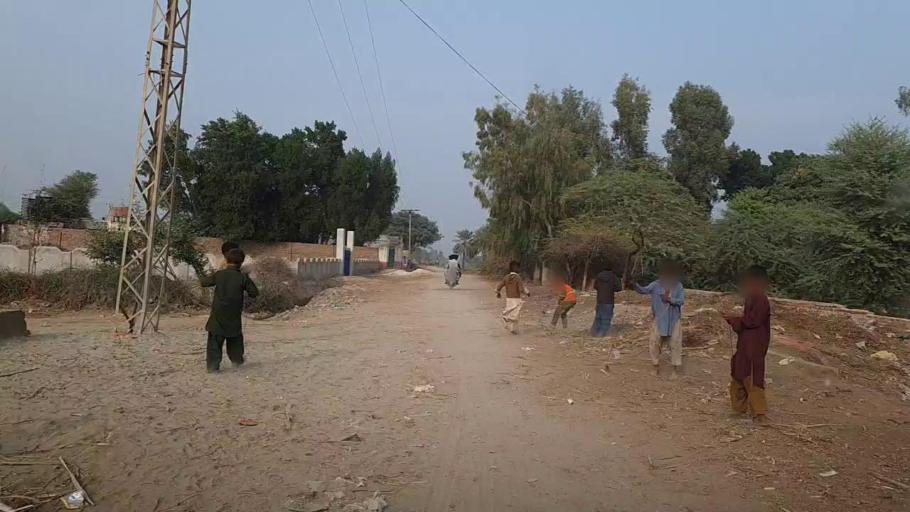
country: PK
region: Sindh
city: Setharja Old
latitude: 27.0891
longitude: 68.4972
